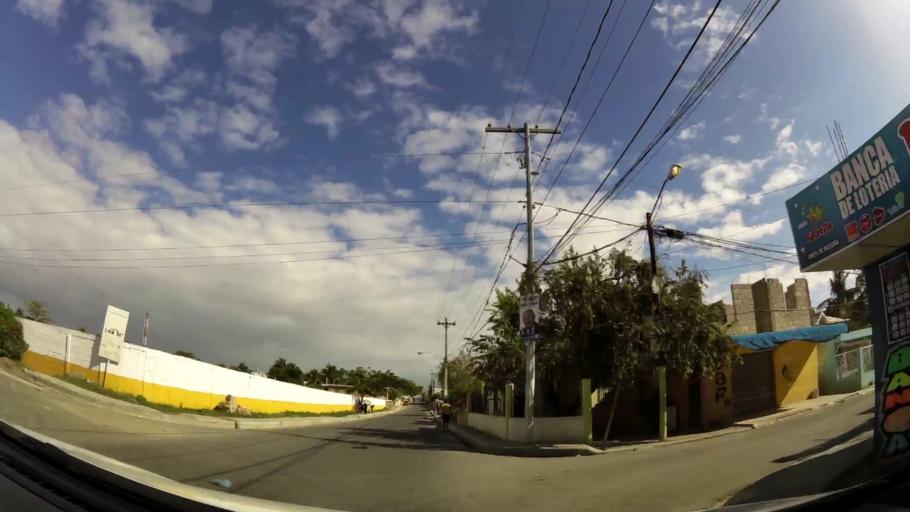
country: DO
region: Santo Domingo
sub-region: Santo Domingo
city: Boca Chica
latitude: 18.4579
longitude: -69.6054
